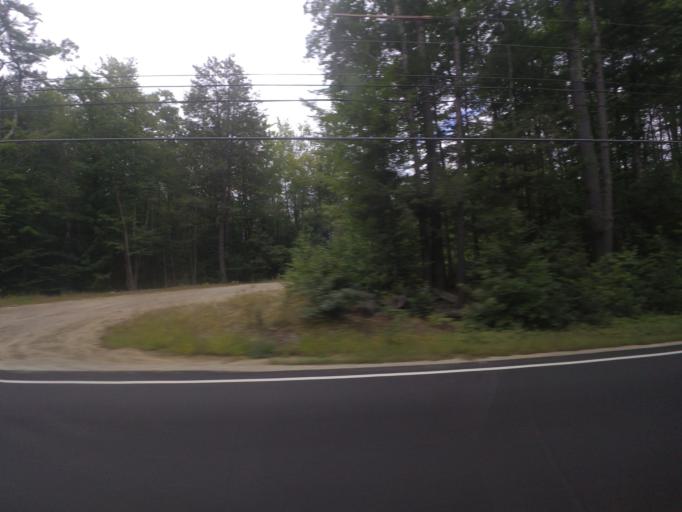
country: US
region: New Hampshire
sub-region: Rockingham County
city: Northwood
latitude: 43.1978
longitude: -71.1317
